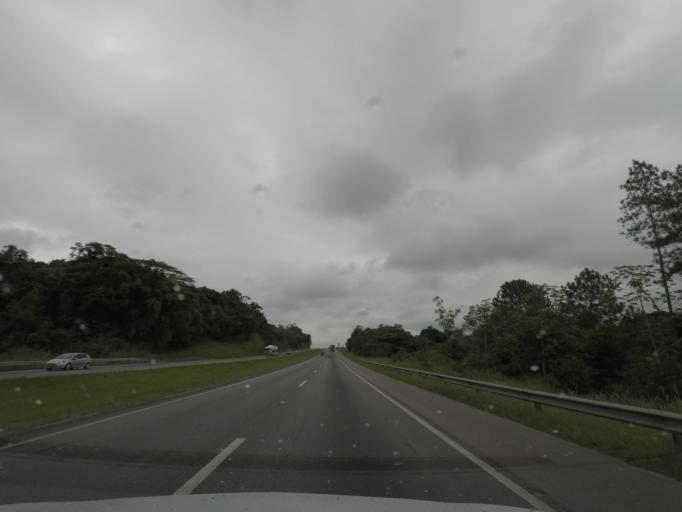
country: BR
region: Sao Paulo
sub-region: Registro
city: Registro
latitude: -24.4492
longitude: -47.8071
